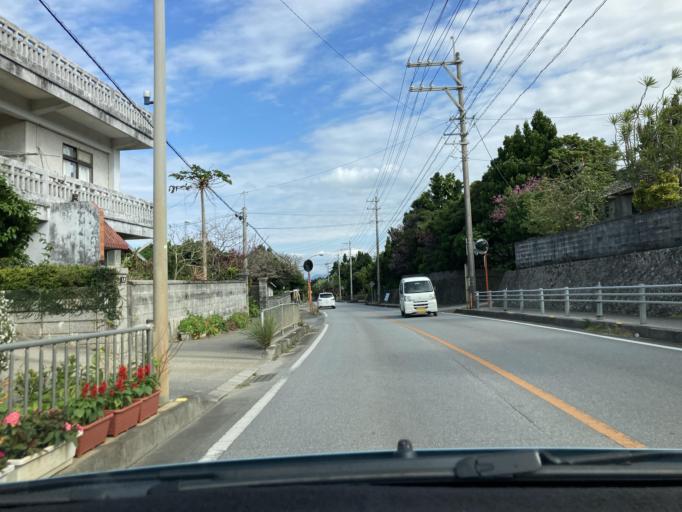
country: JP
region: Okinawa
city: Nago
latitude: 26.6966
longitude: 127.9371
